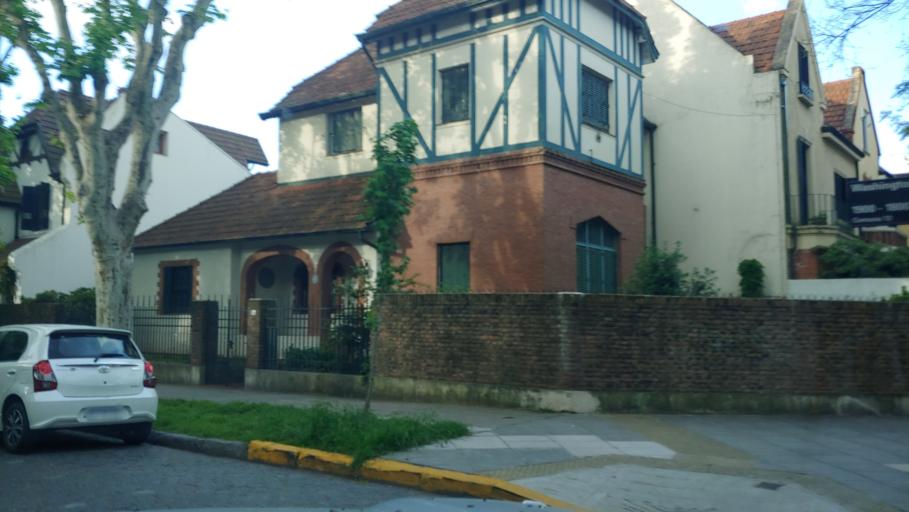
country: AR
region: Buenos Aires F.D.
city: Colegiales
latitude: -34.5723
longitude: -58.4672
